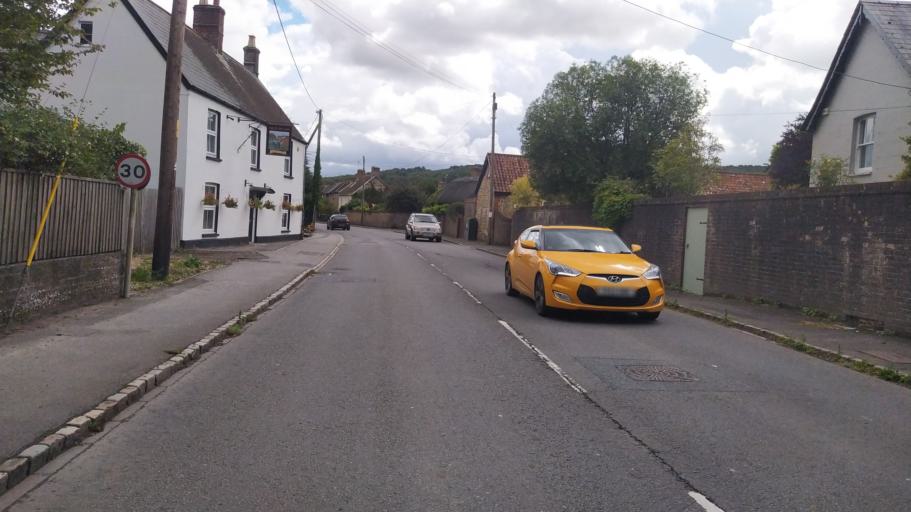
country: GB
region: England
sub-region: Dorset
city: Manston
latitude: 50.8974
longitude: -2.2469
